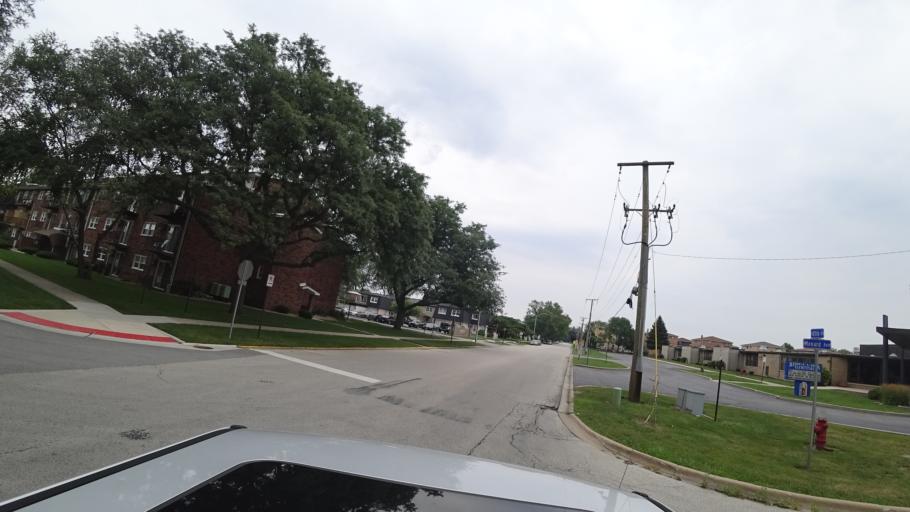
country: US
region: Illinois
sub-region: Cook County
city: Oak Lawn
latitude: 41.7015
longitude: -87.7645
